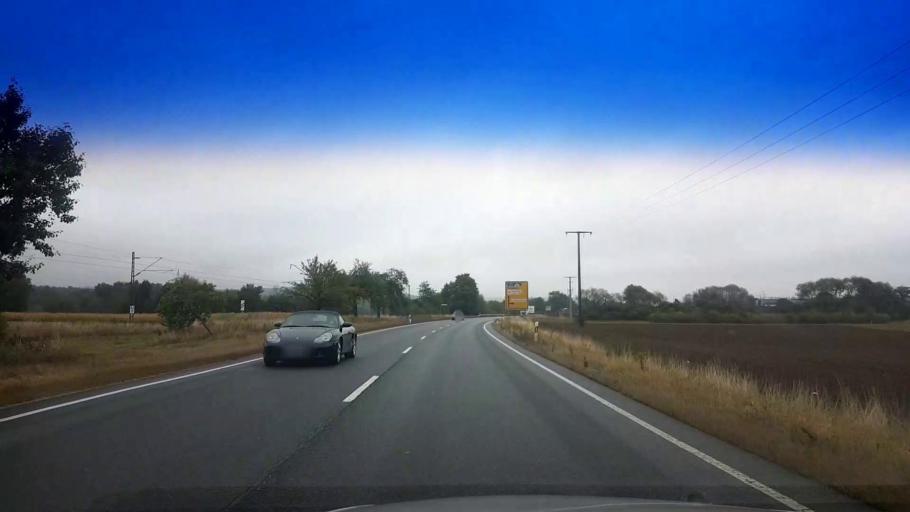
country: DE
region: Bavaria
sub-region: Upper Franconia
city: Eggolsheim
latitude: 49.7581
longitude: 11.0516
